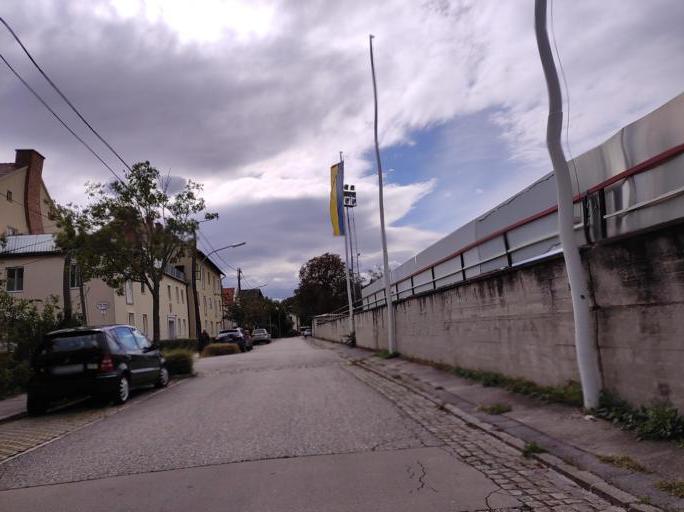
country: AT
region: Lower Austria
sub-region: Politischer Bezirk Baden
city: Baden
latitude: 48.0053
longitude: 16.2470
